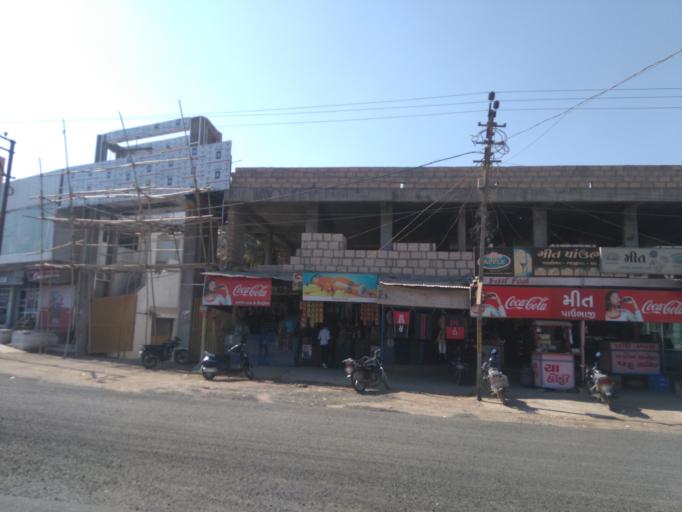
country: IN
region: Gujarat
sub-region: Junagadh
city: Junagadh
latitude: 21.5421
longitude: 70.4642
